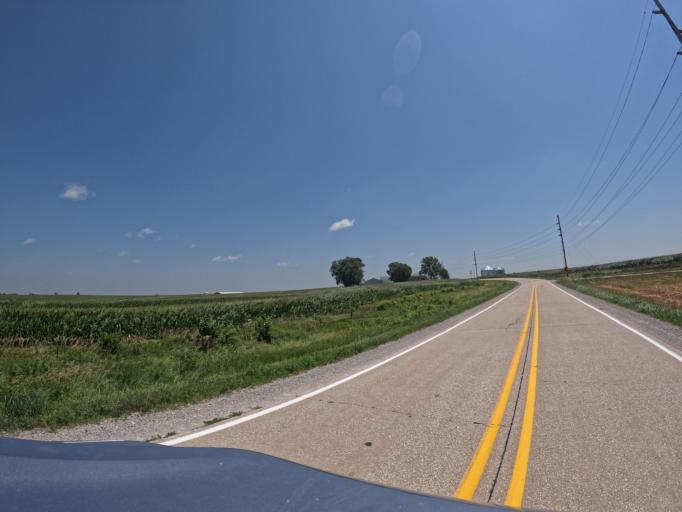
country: US
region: Iowa
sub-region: Keokuk County
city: Sigourney
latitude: 41.2752
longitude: -92.1595
